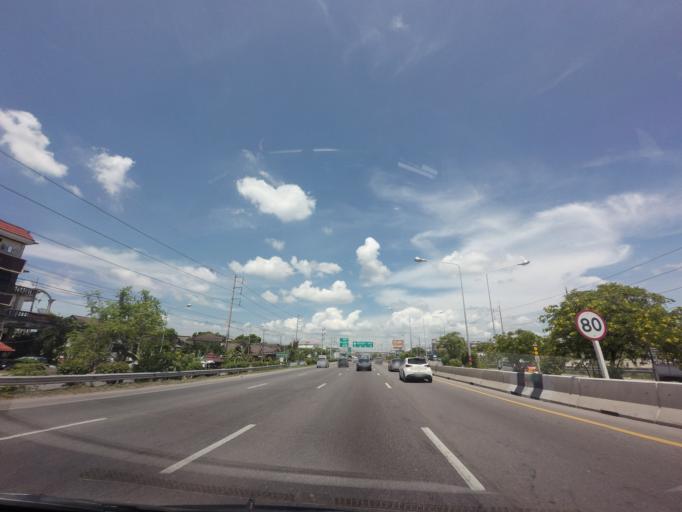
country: TH
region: Samut Sakhon
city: Samut Sakhon
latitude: 13.5252
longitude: 100.1869
